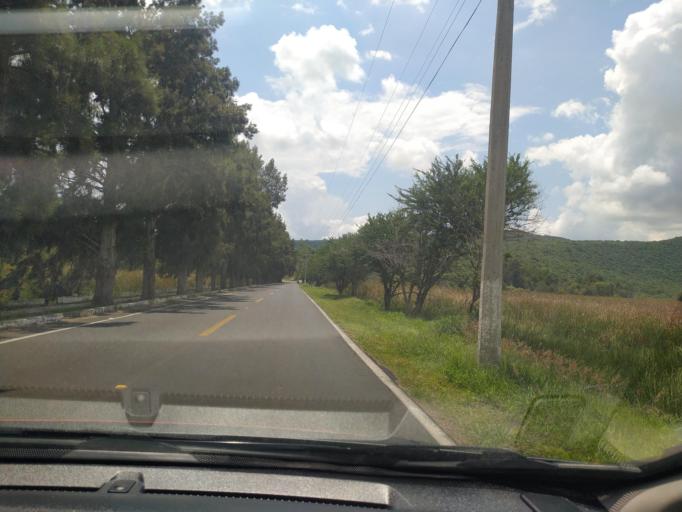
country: MX
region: Jalisco
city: Villa Corona
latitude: 20.4119
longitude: -103.6762
